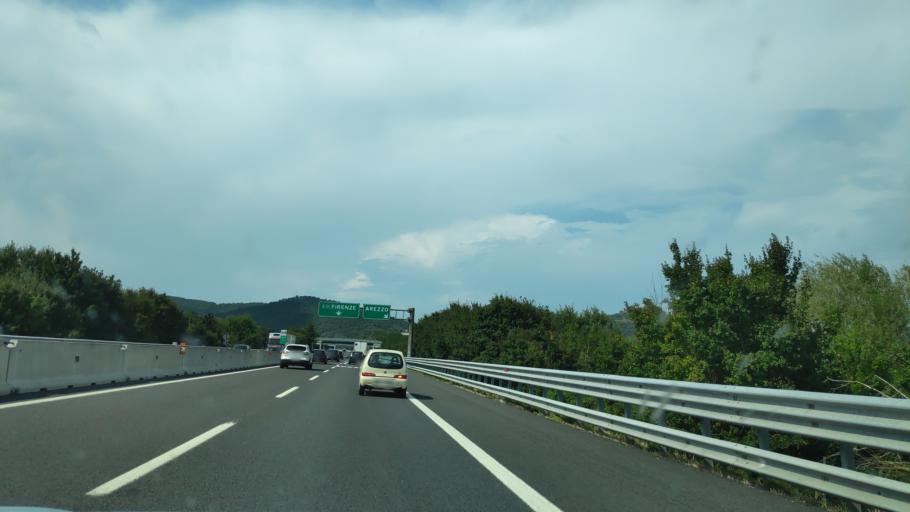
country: IT
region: Tuscany
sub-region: Province of Arezzo
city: Viciomaggio
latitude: 43.4343
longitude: 11.7770
